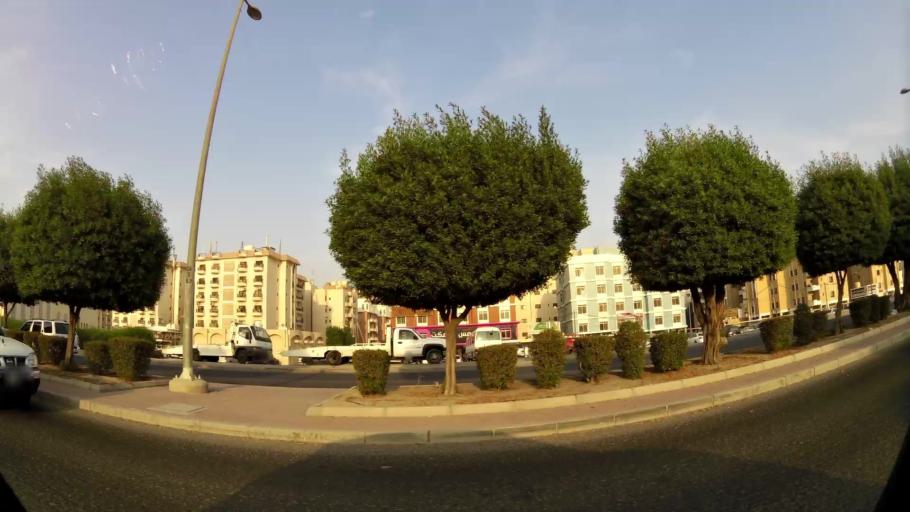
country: KW
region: Mubarak al Kabir
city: Sabah as Salim
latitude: 29.2519
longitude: 48.0798
